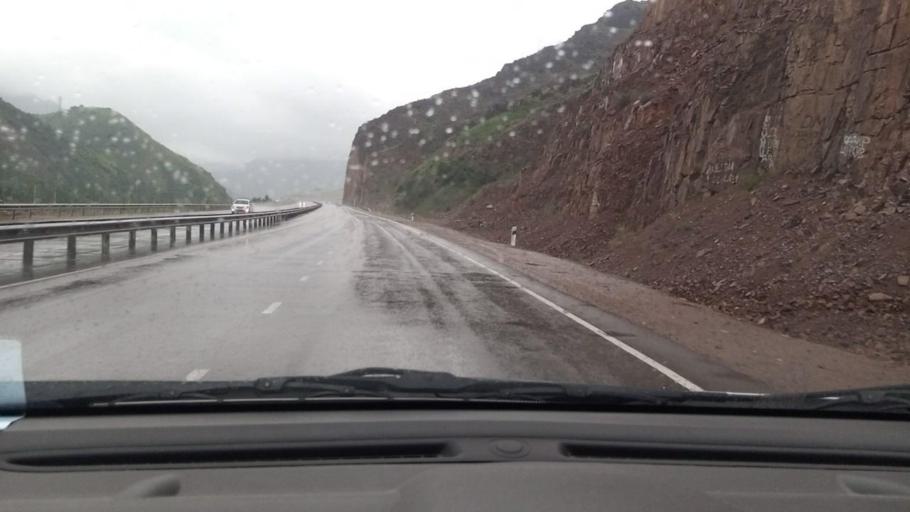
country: UZ
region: Toshkent
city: Angren
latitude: 41.1226
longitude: 70.3514
